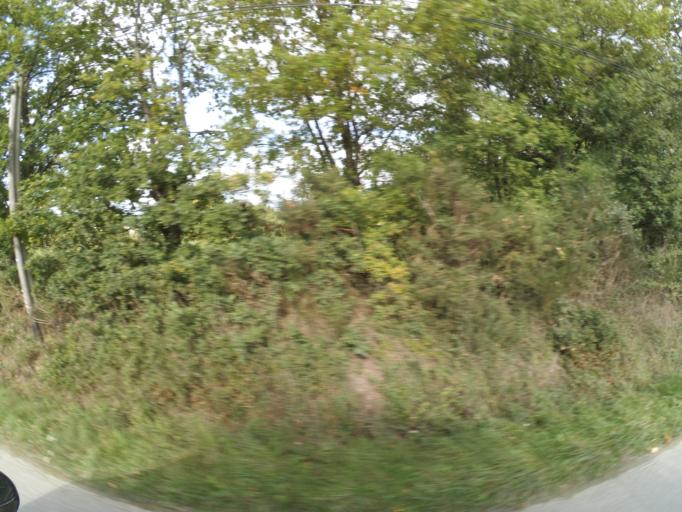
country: FR
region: Pays de la Loire
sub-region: Departement de la Loire-Atlantique
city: Casson
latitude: 47.3989
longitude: -1.5702
